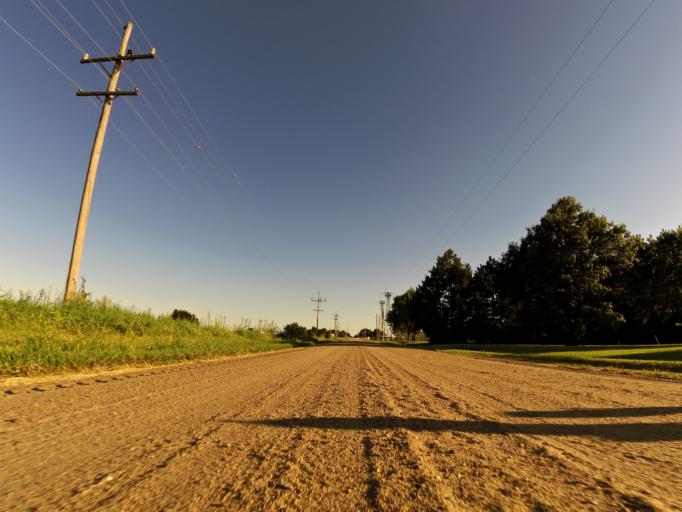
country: US
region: Kansas
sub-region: Reno County
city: South Hutchinson
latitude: 38.0007
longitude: -98.0319
